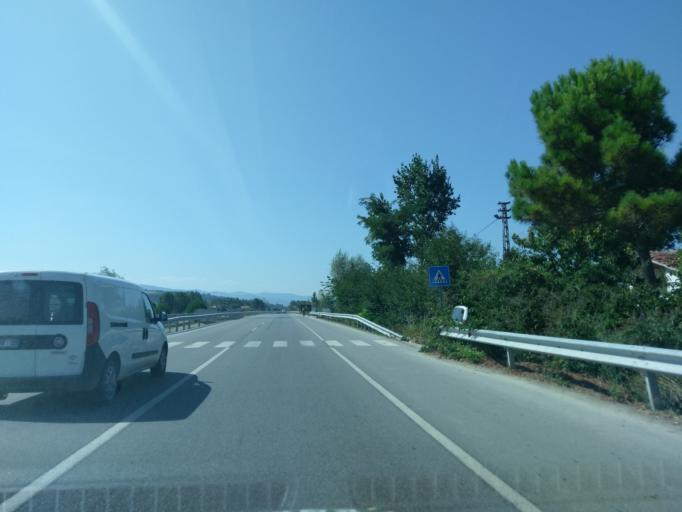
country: TR
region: Samsun
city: Alacam
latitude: 41.6089
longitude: 35.6610
